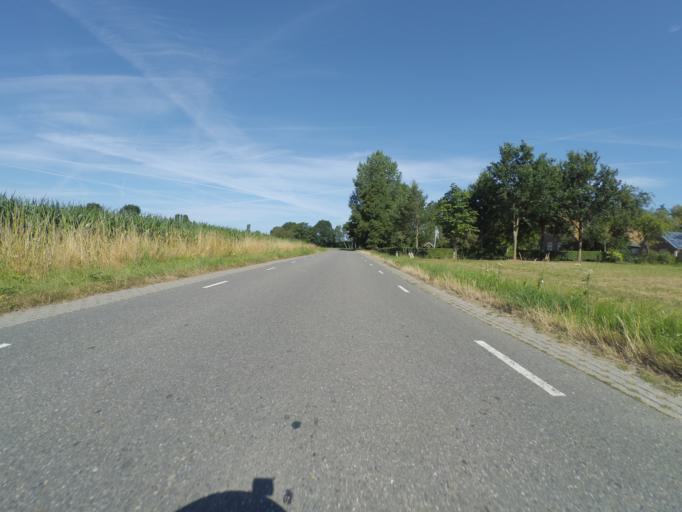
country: NL
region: Gelderland
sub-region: Gemeente Epe
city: Vaassen
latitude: 52.2550
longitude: 6.0215
